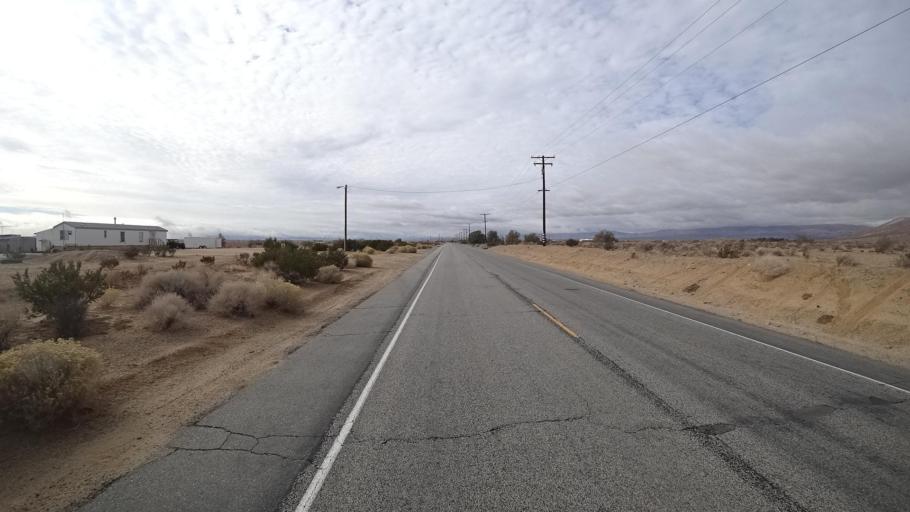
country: US
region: California
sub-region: Kern County
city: Rosamond
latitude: 34.8635
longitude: -118.2781
